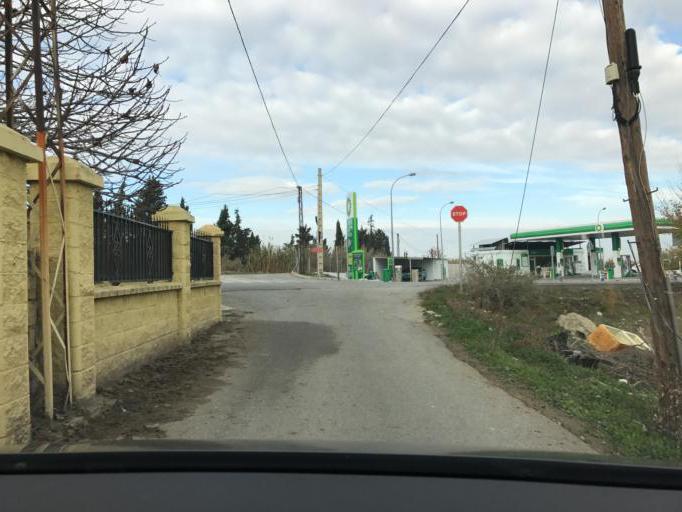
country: ES
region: Andalusia
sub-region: Provincia de Granada
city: Ogijares
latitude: 37.1327
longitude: -3.6030
